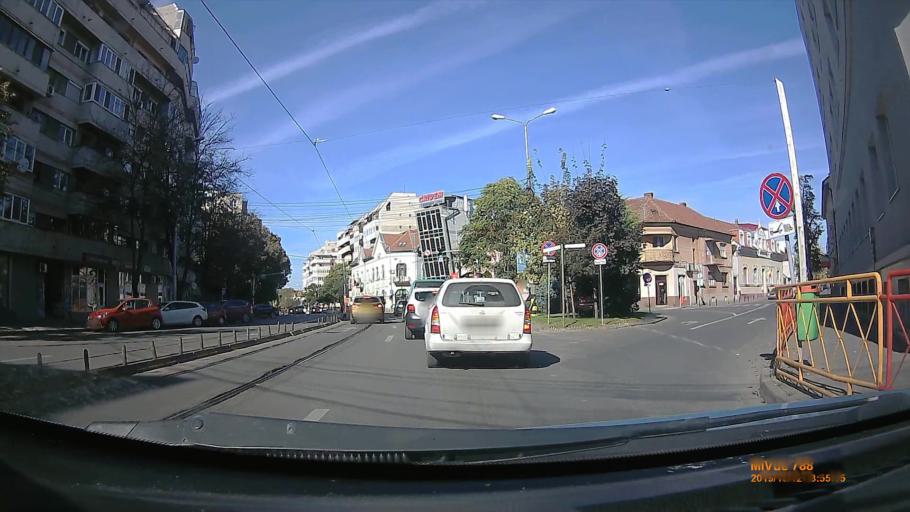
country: RO
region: Bihor
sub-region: Comuna Biharea
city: Oradea
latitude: 47.0584
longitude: 21.9402
